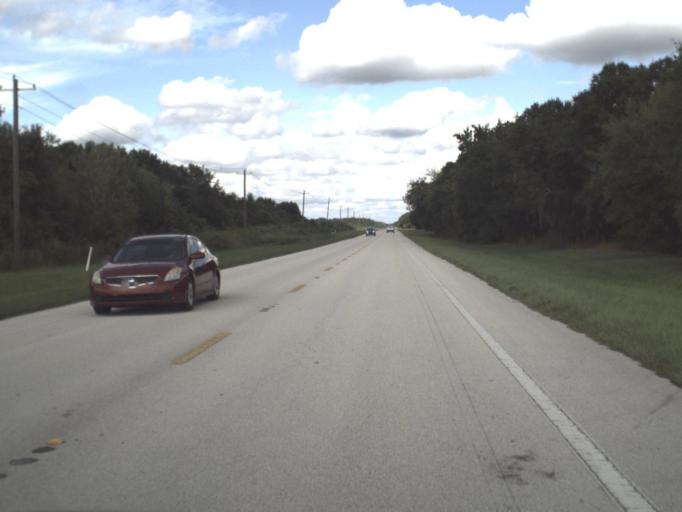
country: US
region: Florida
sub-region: Hillsborough County
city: Ruskin
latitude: 27.6045
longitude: -82.4207
